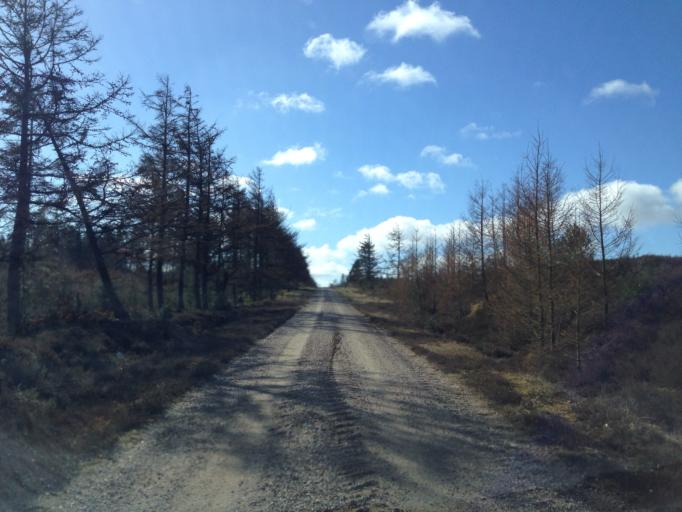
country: DK
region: Central Jutland
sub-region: Holstebro Kommune
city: Ulfborg
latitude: 56.2645
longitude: 8.4625
